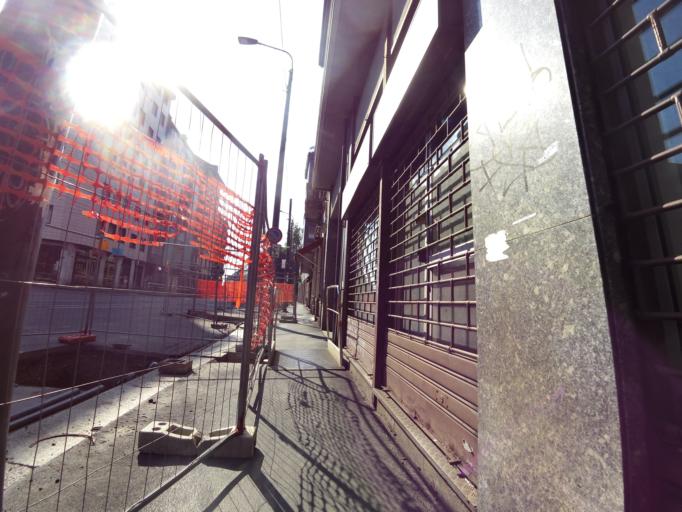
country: IT
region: Lombardy
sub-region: Citta metropolitana di Milano
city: Milano
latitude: 45.4517
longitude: 9.1880
